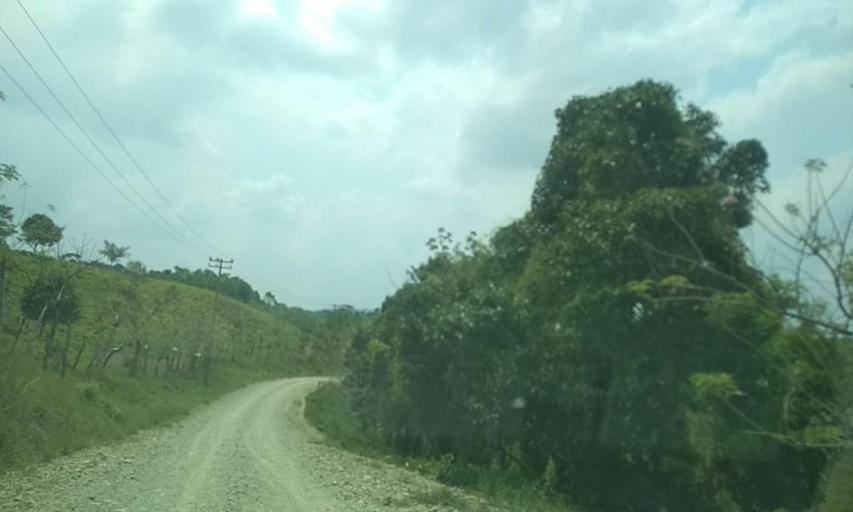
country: MX
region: Tabasco
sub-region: Huimanguillo
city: Francisco Rueda
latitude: 17.6250
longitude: -93.8176
